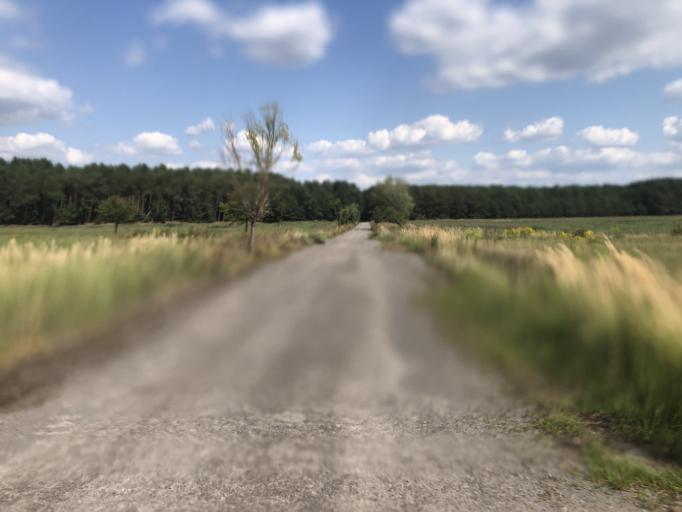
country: DE
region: Brandenburg
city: Mullrose
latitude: 52.2316
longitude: 14.3958
